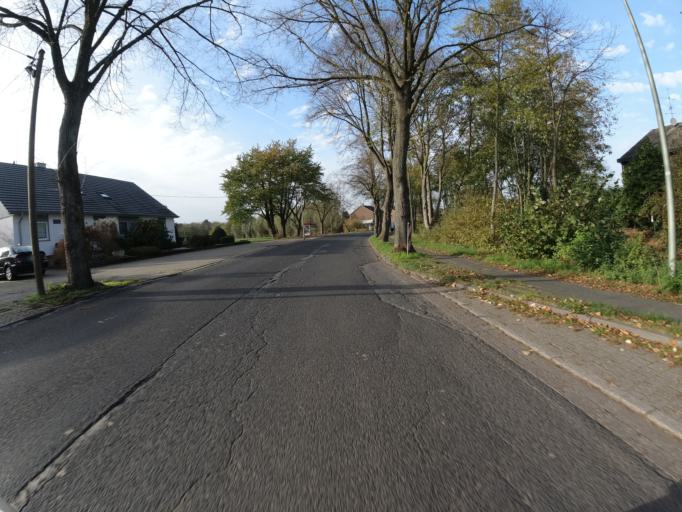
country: DE
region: North Rhine-Westphalia
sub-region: Regierungsbezirk Dusseldorf
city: Moers
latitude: 51.3930
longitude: 6.6736
